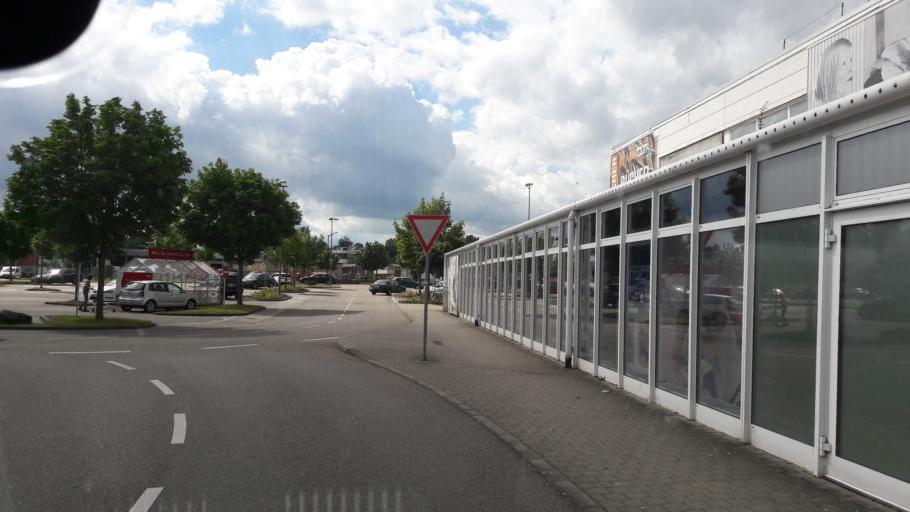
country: DE
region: Baden-Wuerttemberg
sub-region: Regierungsbezirk Stuttgart
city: Ohringen
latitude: 49.2058
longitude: 9.4888
